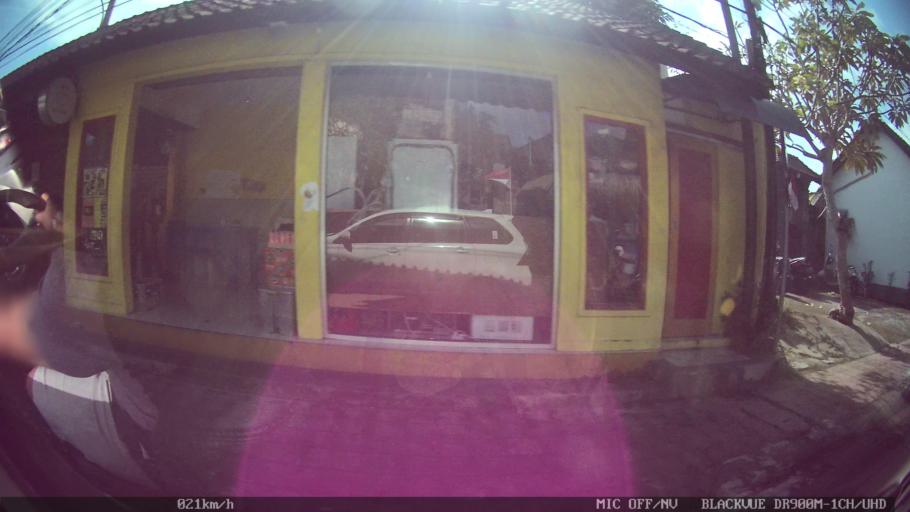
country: ID
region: Bali
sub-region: Kabupaten Gianyar
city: Ubud
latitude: -8.5112
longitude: 115.2686
